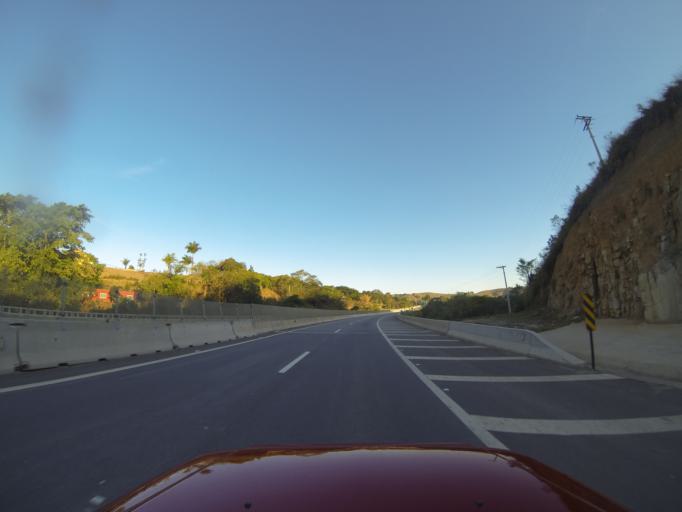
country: BR
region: Sao Paulo
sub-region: Santa Branca
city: Santa Branca
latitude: -23.4137
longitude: -45.6403
